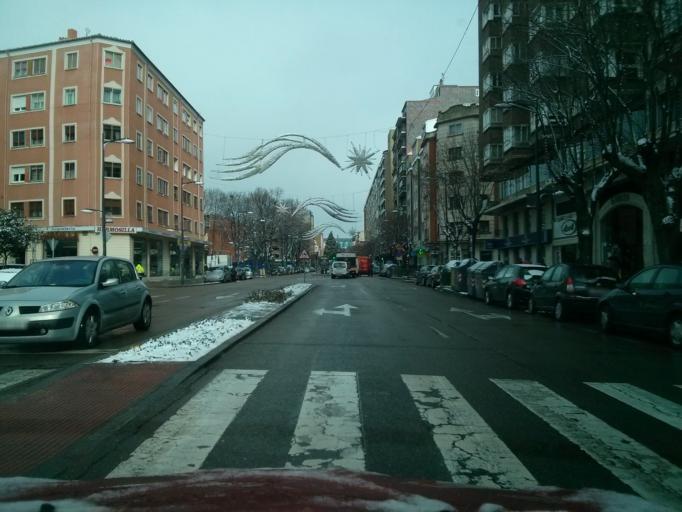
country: ES
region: Castille and Leon
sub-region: Provincia de Burgos
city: Burgos
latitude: 42.3447
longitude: -3.6983
